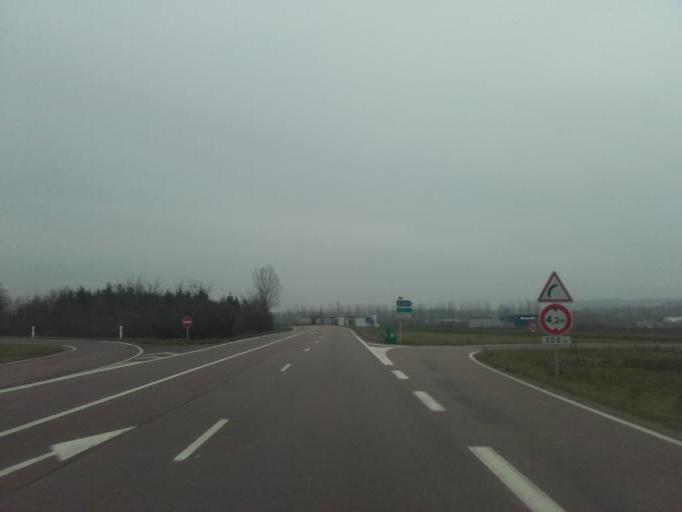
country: FR
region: Bourgogne
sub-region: Departement de la Cote-d'Or
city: Corpeau
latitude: 46.9267
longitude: 4.7430
